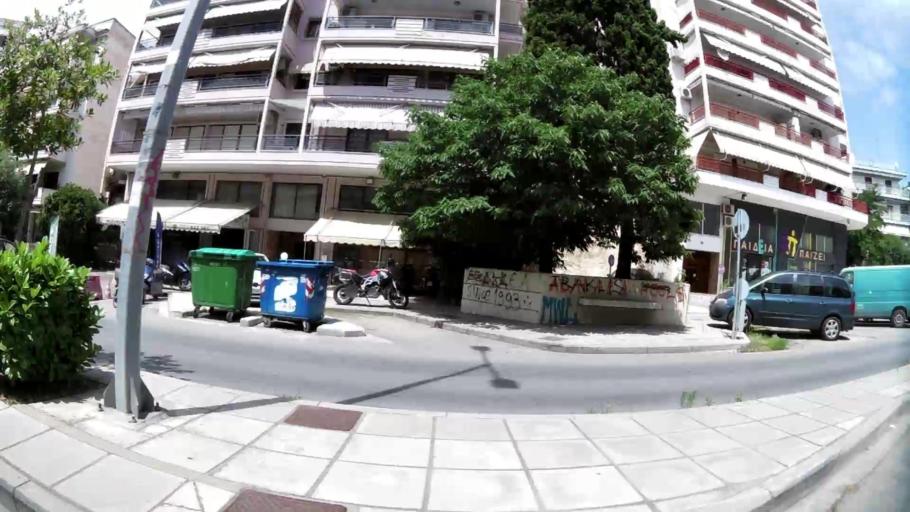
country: GR
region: Central Macedonia
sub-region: Nomos Thessalonikis
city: Triandria
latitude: 40.6186
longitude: 22.9656
